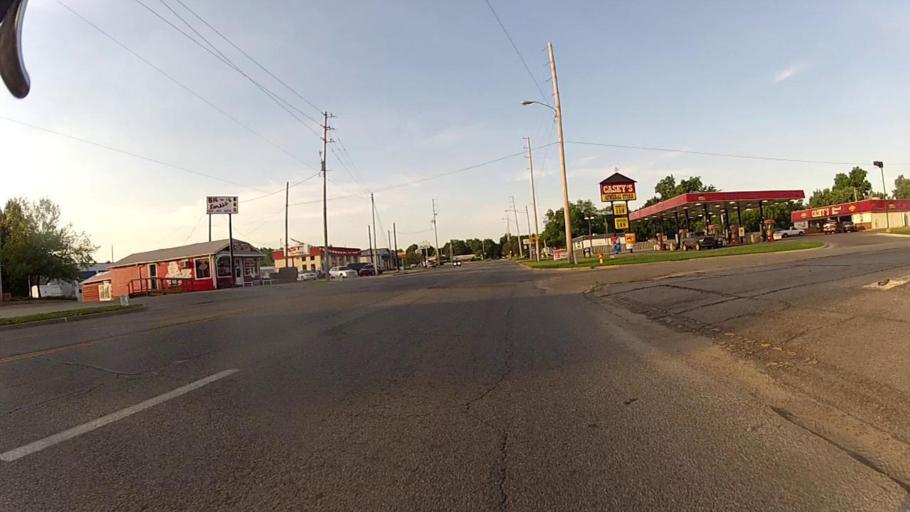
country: US
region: Kansas
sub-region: Cowley County
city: Arkansas City
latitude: 37.0799
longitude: -97.0401
